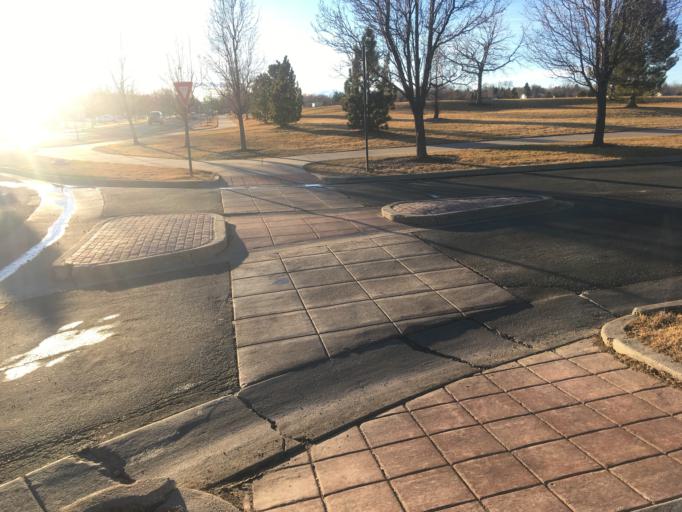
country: US
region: Colorado
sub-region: Broomfield County
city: Broomfield
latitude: 39.9363
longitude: -105.0489
